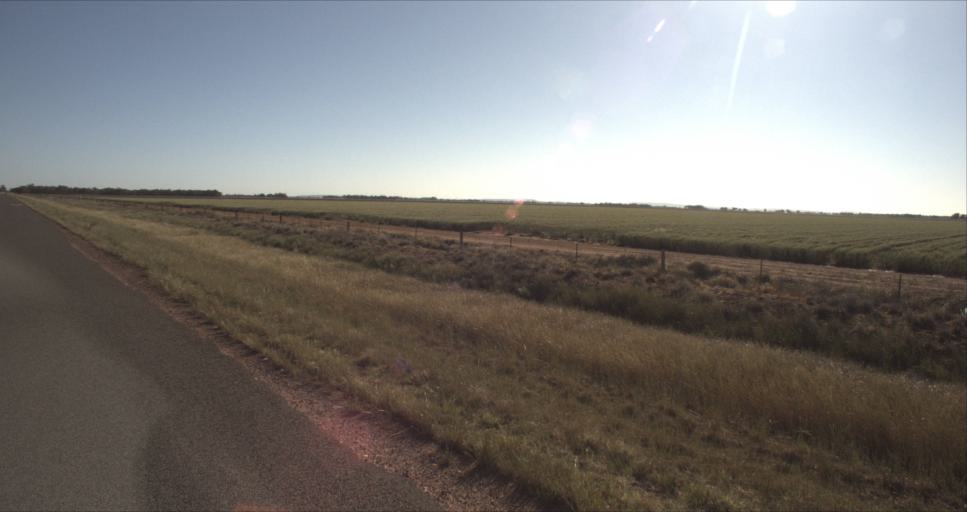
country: AU
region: New South Wales
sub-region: Leeton
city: Leeton
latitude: -34.5754
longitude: 146.2627
